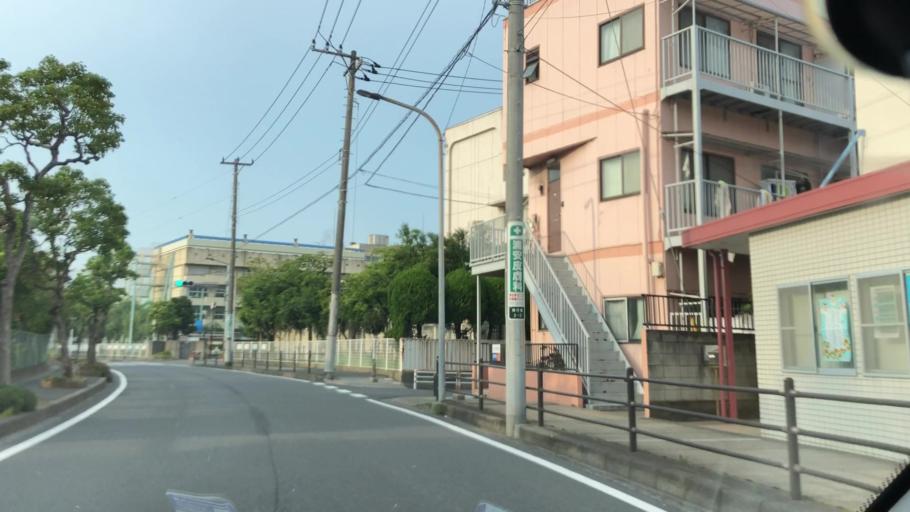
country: JP
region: Tokyo
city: Urayasu
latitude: 35.6707
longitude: 139.9060
